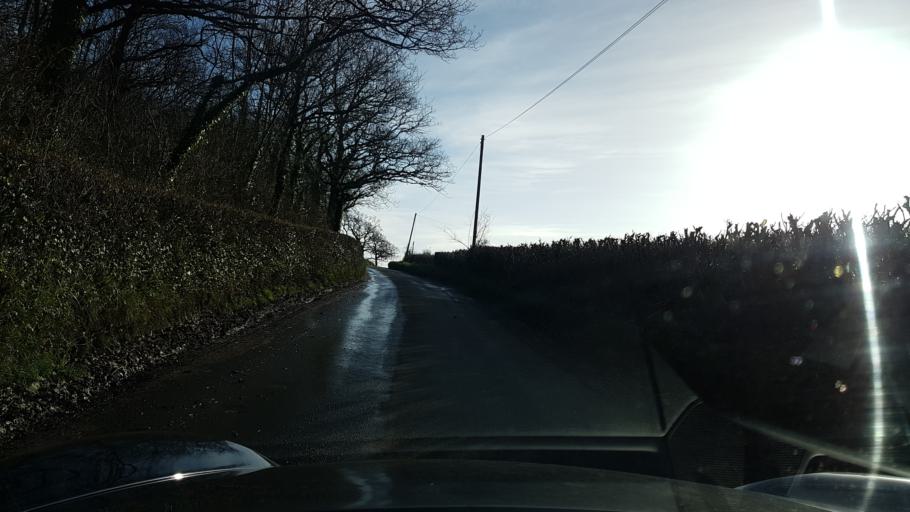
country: GB
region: England
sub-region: Dorset
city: Bridport
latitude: 50.7792
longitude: -2.8181
